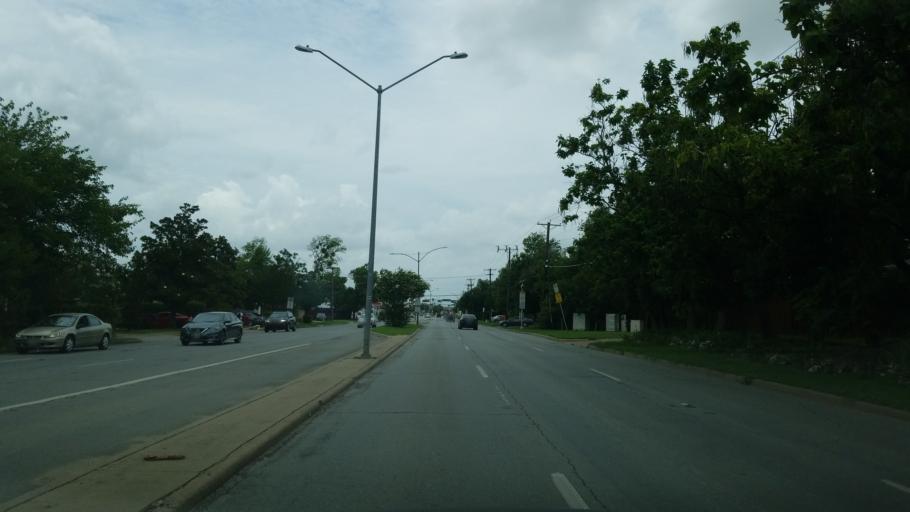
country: US
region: Texas
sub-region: Dallas County
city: Farmers Branch
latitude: 32.8810
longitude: -96.8751
